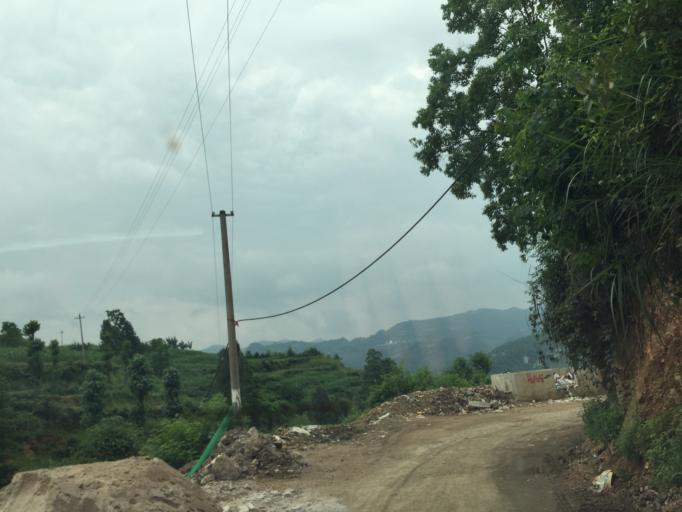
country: CN
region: Guizhou Sheng
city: Tongjing
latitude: 28.3715
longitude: 108.2371
